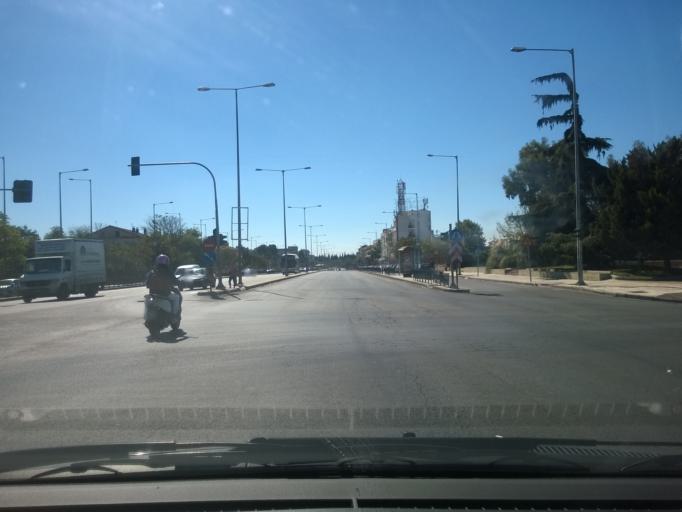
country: GR
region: Central Macedonia
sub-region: Nomos Thessalonikis
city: Stavroupoli
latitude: 40.6620
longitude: 22.9356
